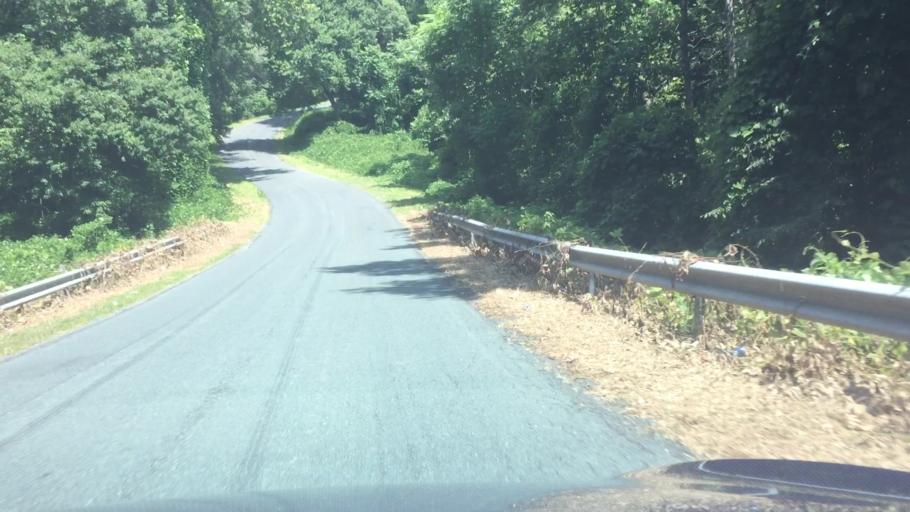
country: US
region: Virginia
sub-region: Appomattox County
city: Appomattox
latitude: 37.3265
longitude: -78.8701
